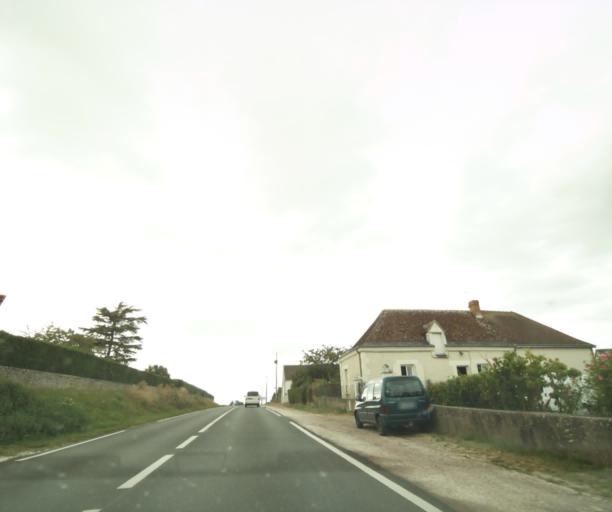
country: FR
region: Centre
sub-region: Departement d'Indre-et-Loire
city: Chambourg-sur-Indre
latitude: 47.1798
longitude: 0.9643
